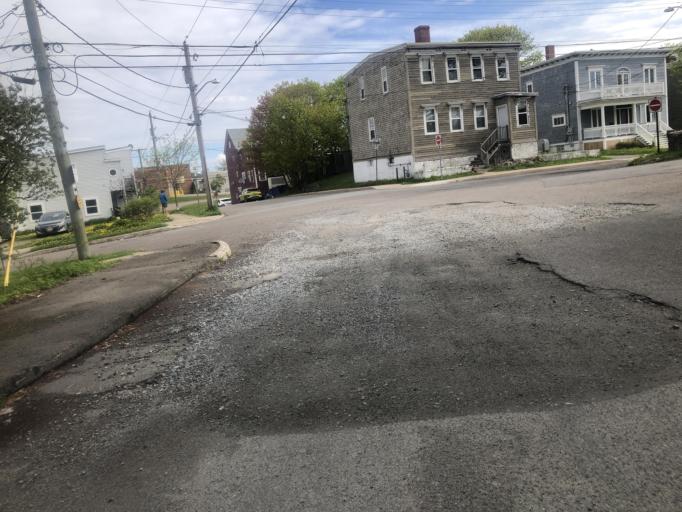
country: CA
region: New Brunswick
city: Saint John
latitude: 45.2744
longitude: -66.0808
